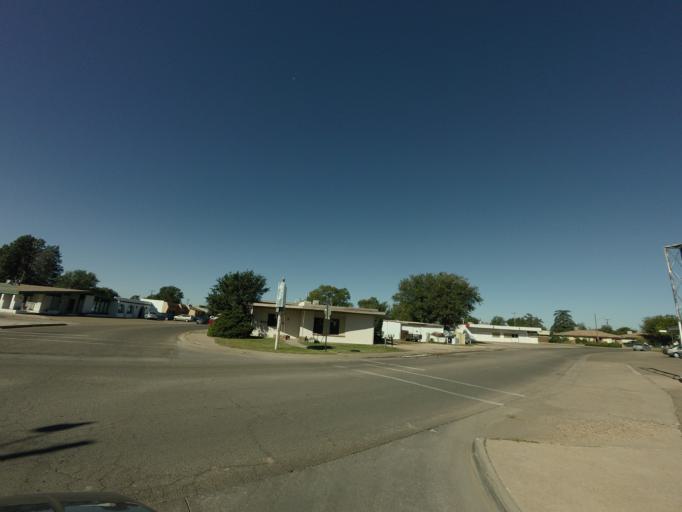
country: US
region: New Mexico
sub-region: Curry County
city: Clovis
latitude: 34.4271
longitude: -103.2071
